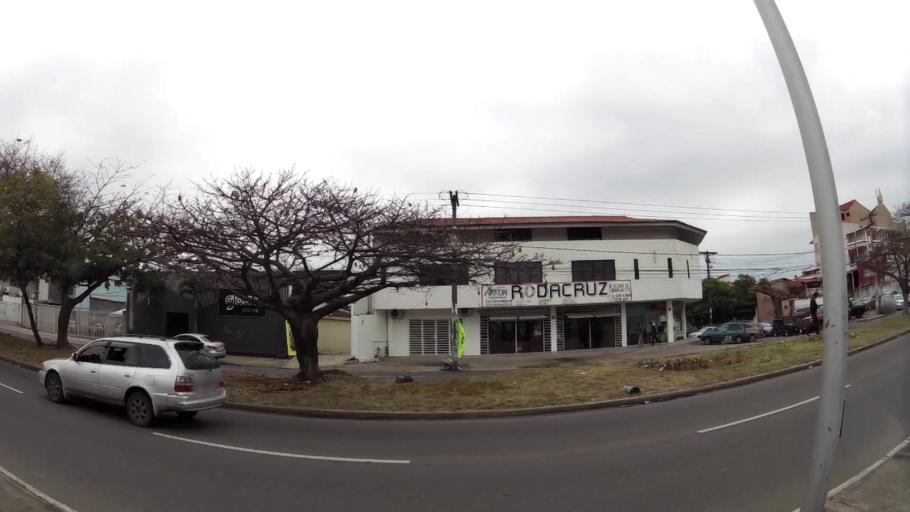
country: BO
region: Santa Cruz
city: Santa Cruz de la Sierra
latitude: -17.7722
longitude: -63.1673
